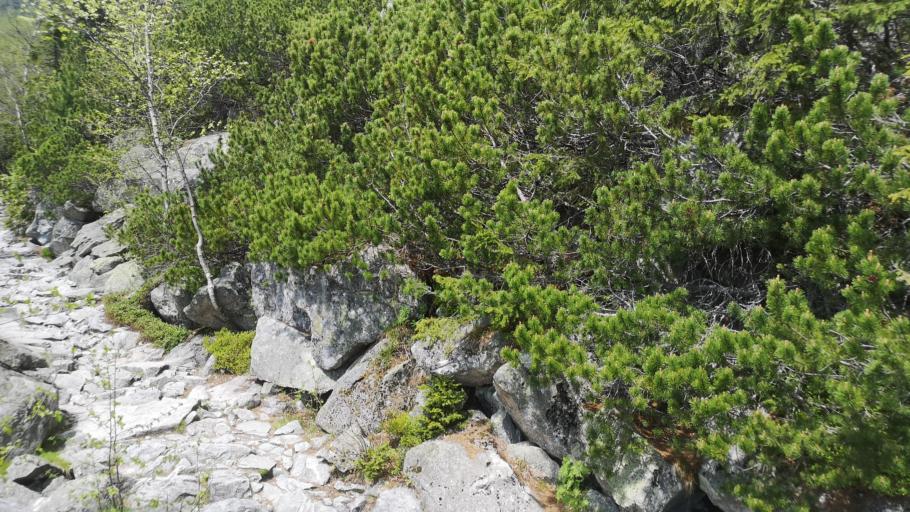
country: SK
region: Presovsky
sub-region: Okres Poprad
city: Vysoke Tatry
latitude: 49.1698
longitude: 20.2240
